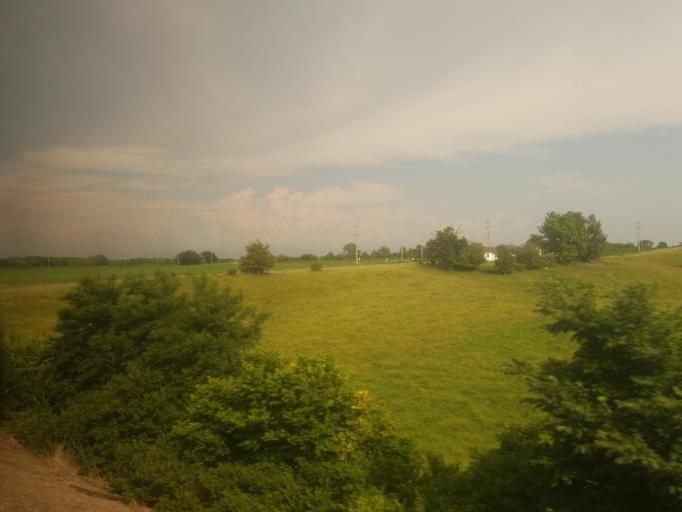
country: US
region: Illinois
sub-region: Bureau County
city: Princeton
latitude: 41.3444
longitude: -89.6278
